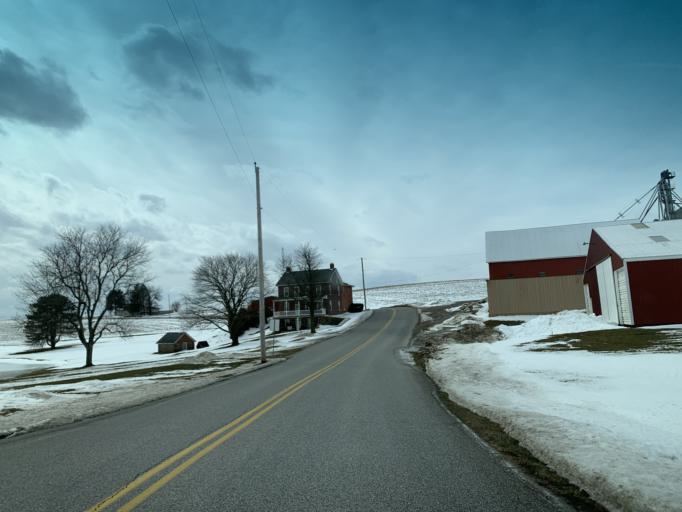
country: US
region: Pennsylvania
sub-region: York County
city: Shrewsbury
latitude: 39.7795
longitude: -76.6449
